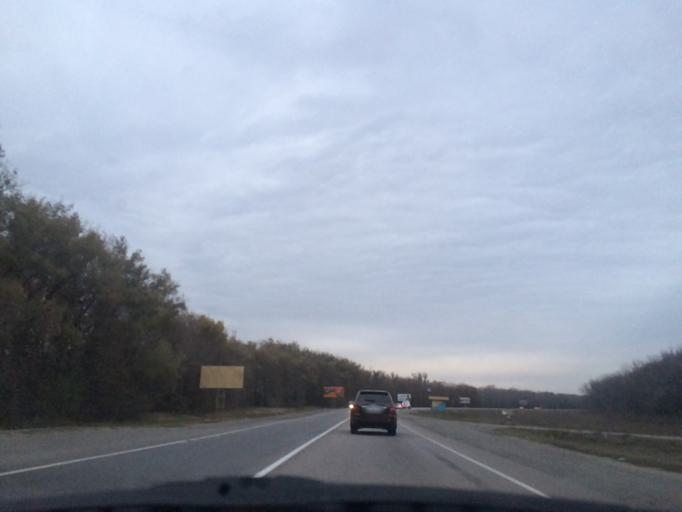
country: RU
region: Rostov
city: Grushevskaya
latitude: 47.4183
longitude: 39.9954
